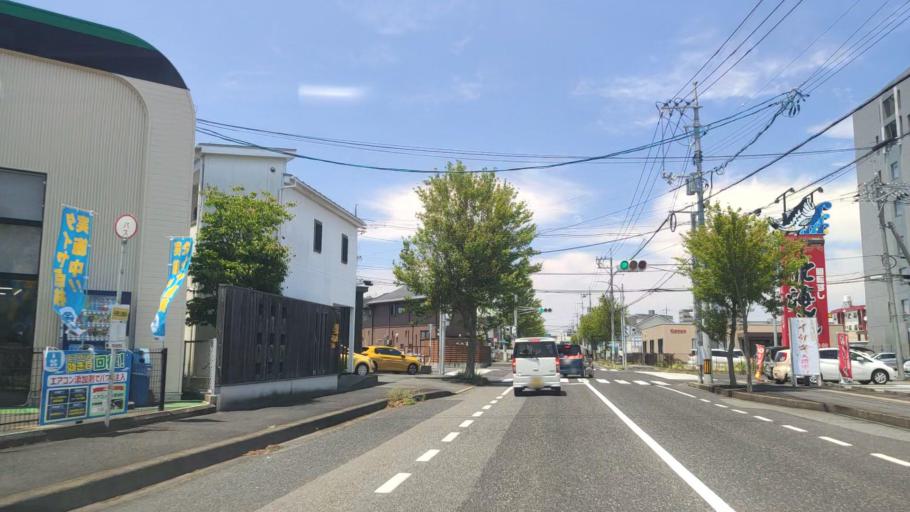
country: JP
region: Tottori
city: Tottori
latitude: 35.4859
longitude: 134.2333
